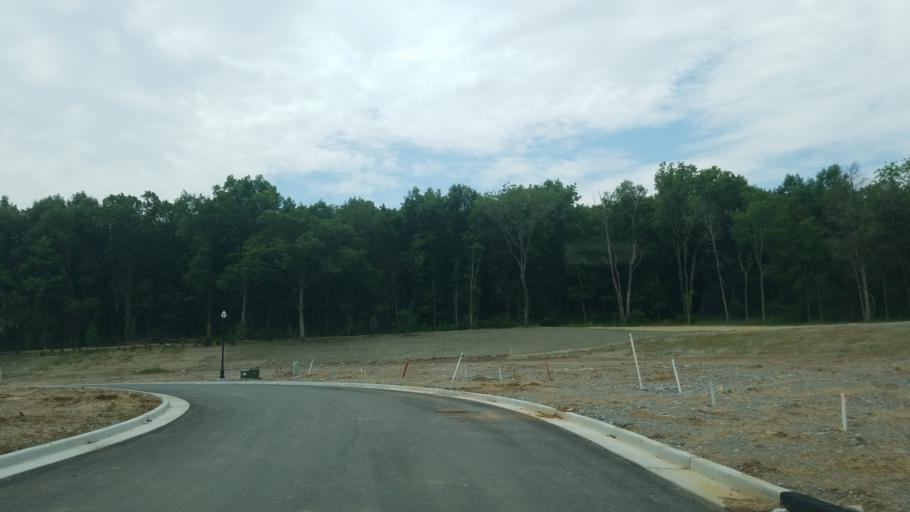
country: US
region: Tennessee
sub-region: Rutherford County
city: La Vergne
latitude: 36.0436
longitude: -86.5986
